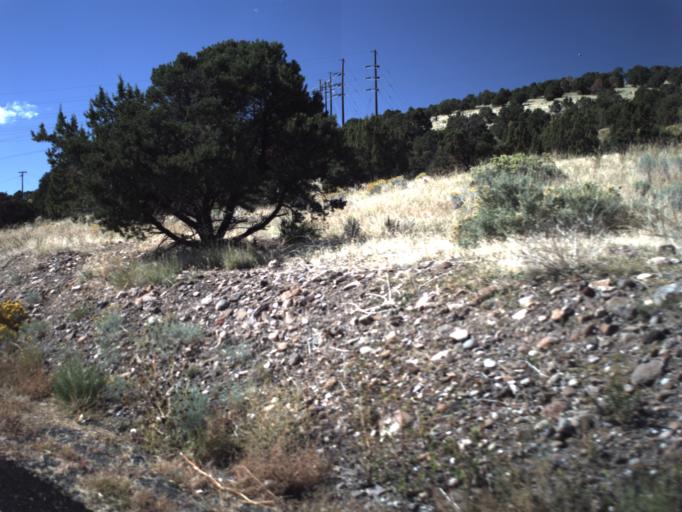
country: US
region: Utah
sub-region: Beaver County
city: Beaver
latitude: 38.2821
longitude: -112.5936
